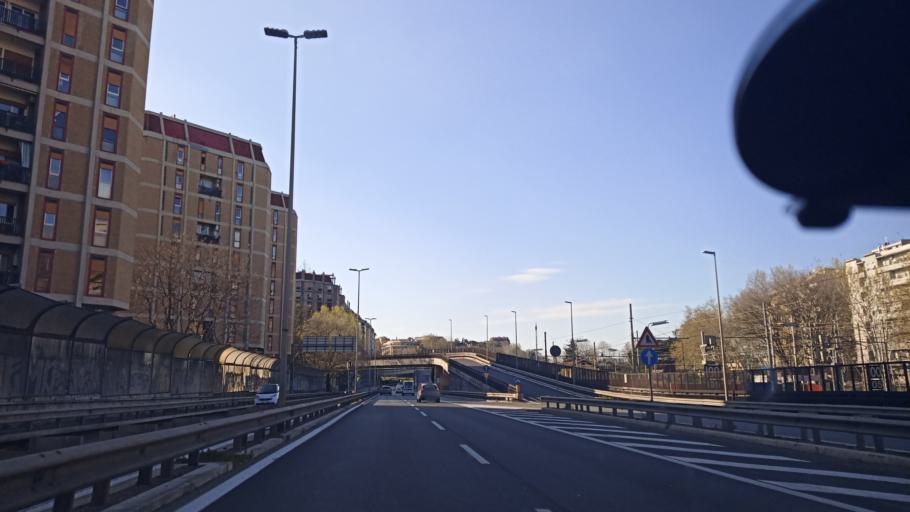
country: IT
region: Latium
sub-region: Citta metropolitana di Roma Capitale
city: Rome
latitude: 41.9313
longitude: 12.5249
